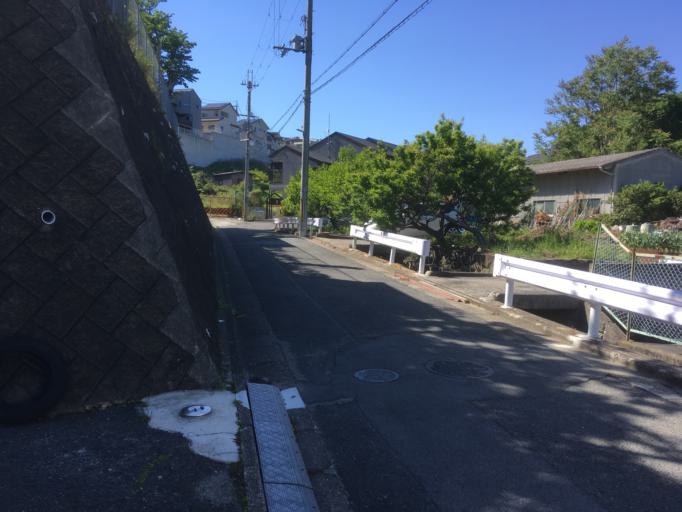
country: JP
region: Nara
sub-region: Ikoma-shi
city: Ikoma
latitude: 34.6862
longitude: 135.6985
